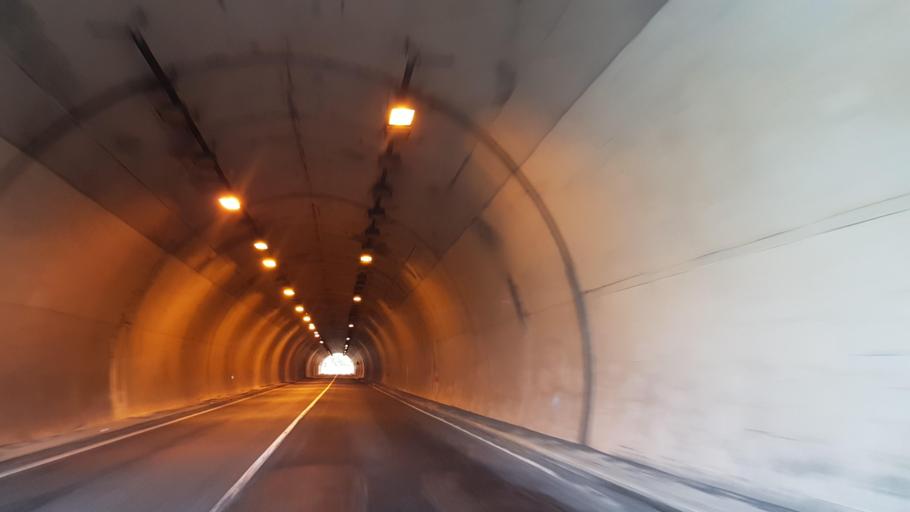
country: IT
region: Emilia-Romagna
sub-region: Provincia di Parma
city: Borgo Val di Taro
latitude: 44.5162
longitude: 9.8416
